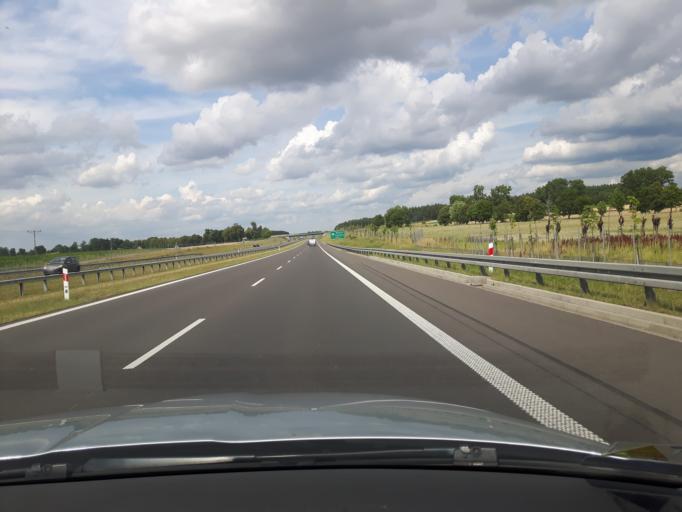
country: PL
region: Warmian-Masurian Voivodeship
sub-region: Powiat nidzicki
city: Nidzica
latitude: 53.3051
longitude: 20.4369
